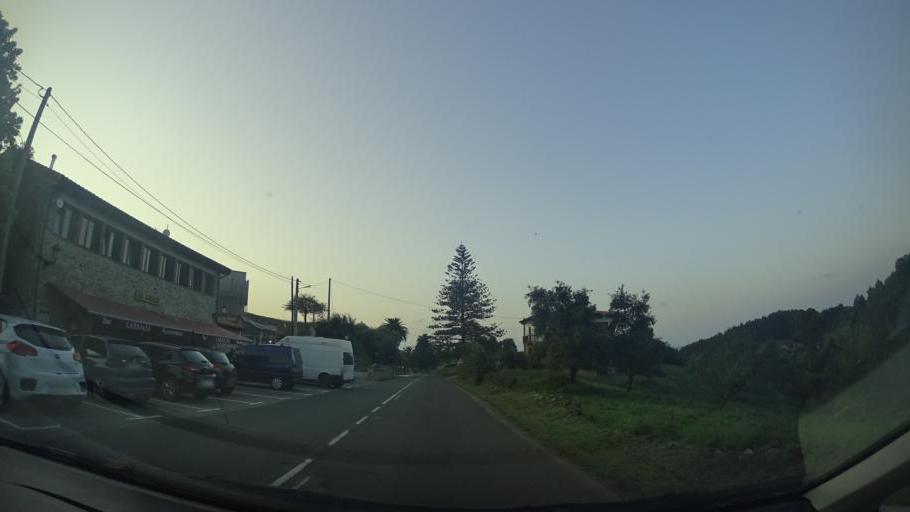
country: ES
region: Asturias
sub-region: Province of Asturias
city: Colunga
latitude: 43.4629
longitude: -5.2019
